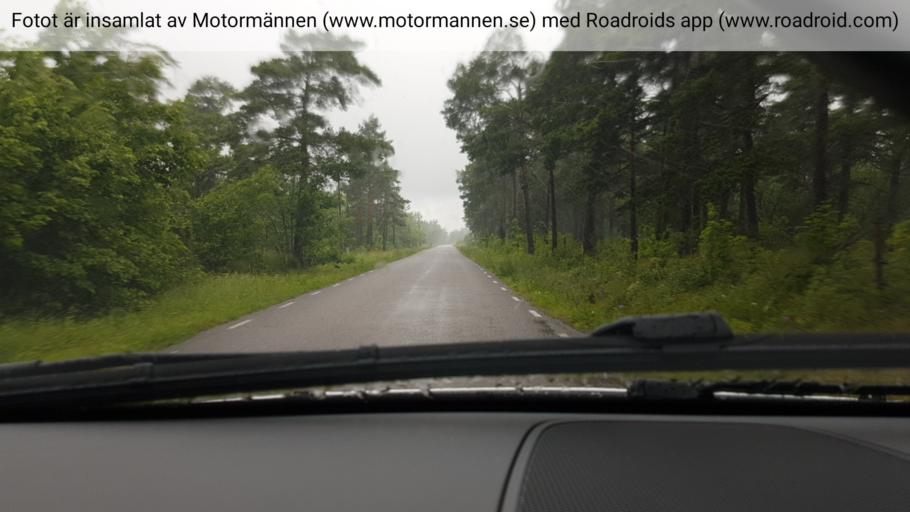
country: SE
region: Gotland
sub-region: Gotland
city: Slite
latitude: 57.8969
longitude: 18.7111
